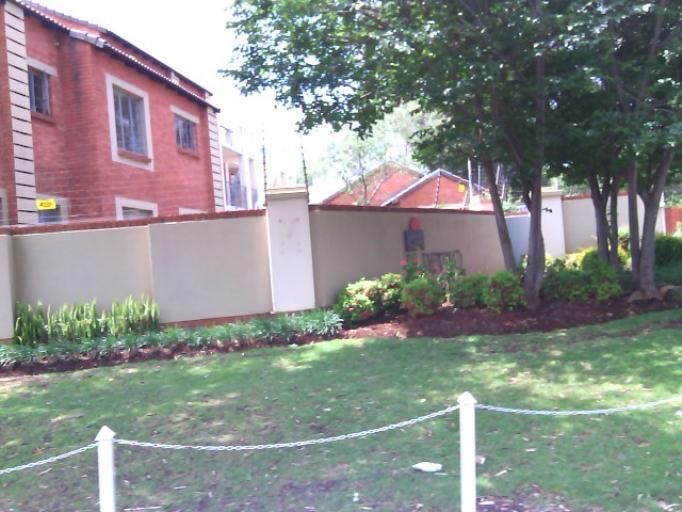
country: ZA
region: Gauteng
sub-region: City of Tshwane Metropolitan Municipality
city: Centurion
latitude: -25.8430
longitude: 28.1862
